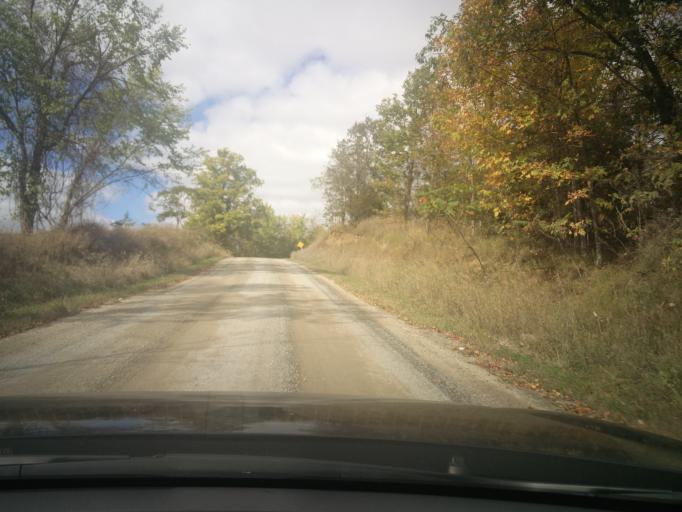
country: CA
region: Ontario
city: Perth
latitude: 44.6590
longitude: -76.5784
